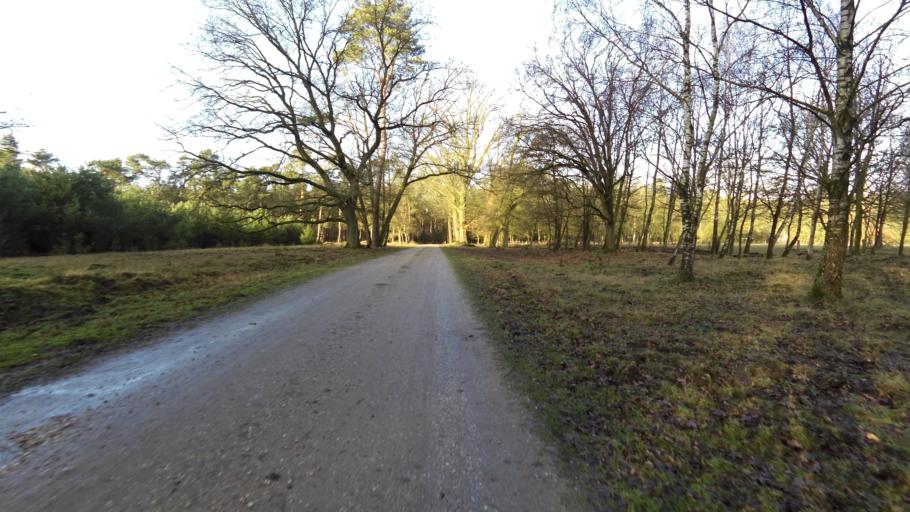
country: NL
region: Gelderland
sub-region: Gemeente Epe
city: Vaassen
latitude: 52.2555
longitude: 5.9165
